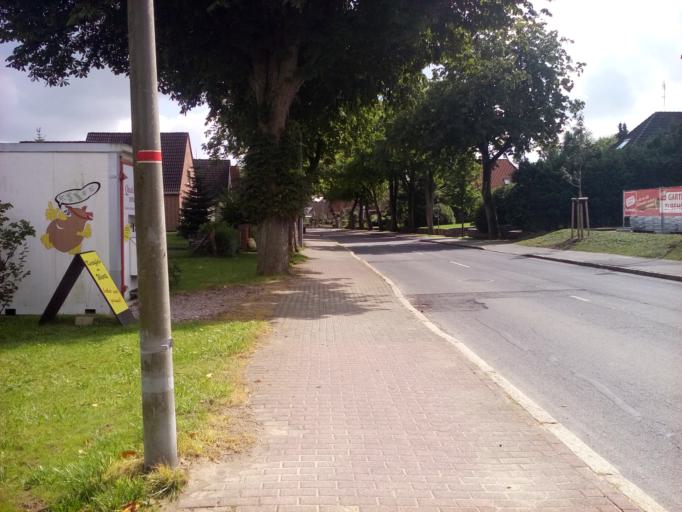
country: DE
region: Schleswig-Holstein
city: Burg
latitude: 54.0057
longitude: 9.2511
